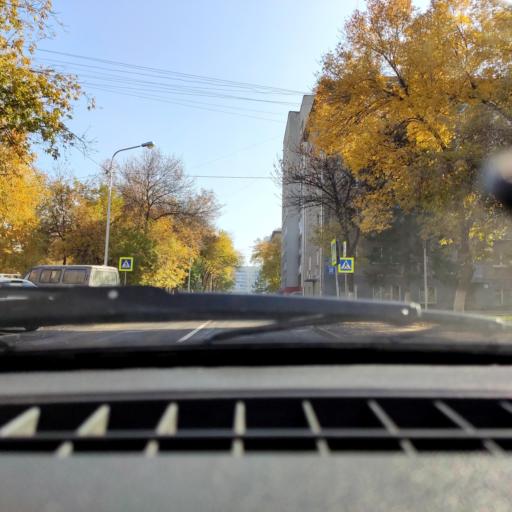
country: RU
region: Bashkortostan
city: Ufa
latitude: 54.7952
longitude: 56.0326
